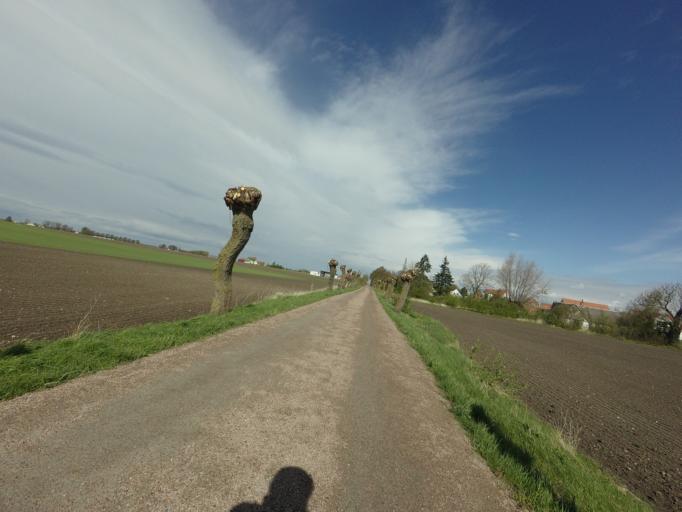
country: SE
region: Skane
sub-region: Malmo
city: Tygelsjo
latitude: 55.5249
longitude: 12.9870
